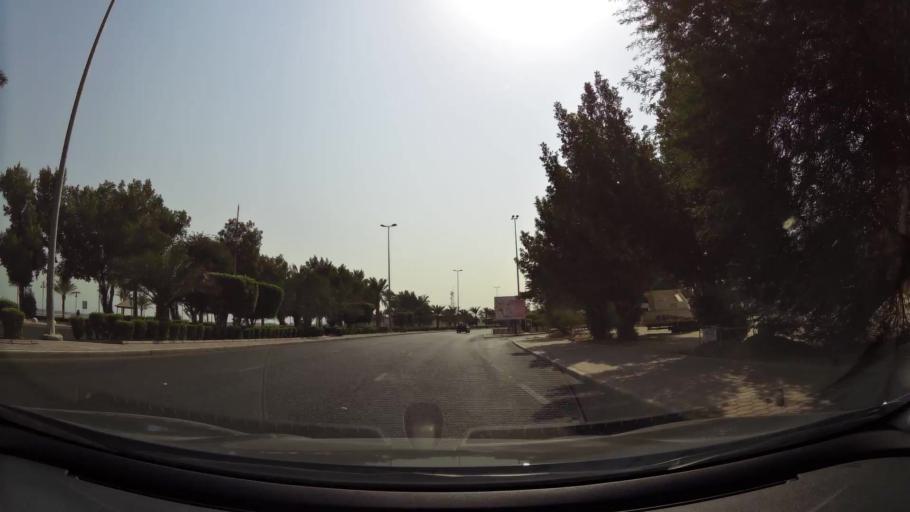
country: KW
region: Al Ahmadi
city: Al Fintas
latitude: 29.1772
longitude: 48.1219
